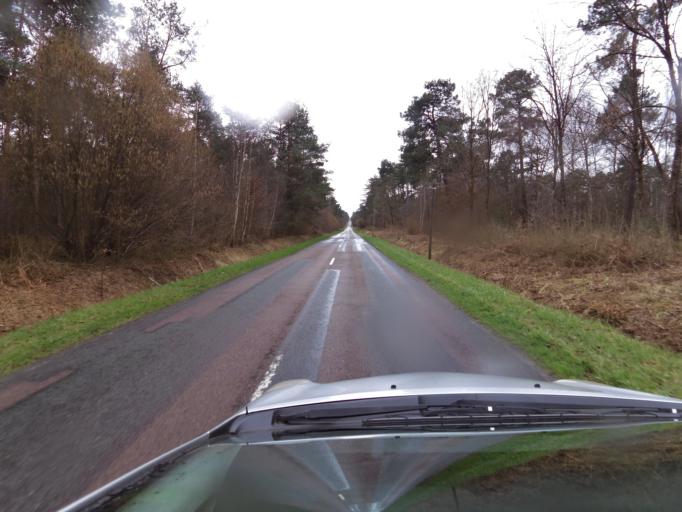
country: FR
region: Picardie
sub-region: Departement de l'Oise
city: Ver-sur-Launette
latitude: 49.1539
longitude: 2.6606
